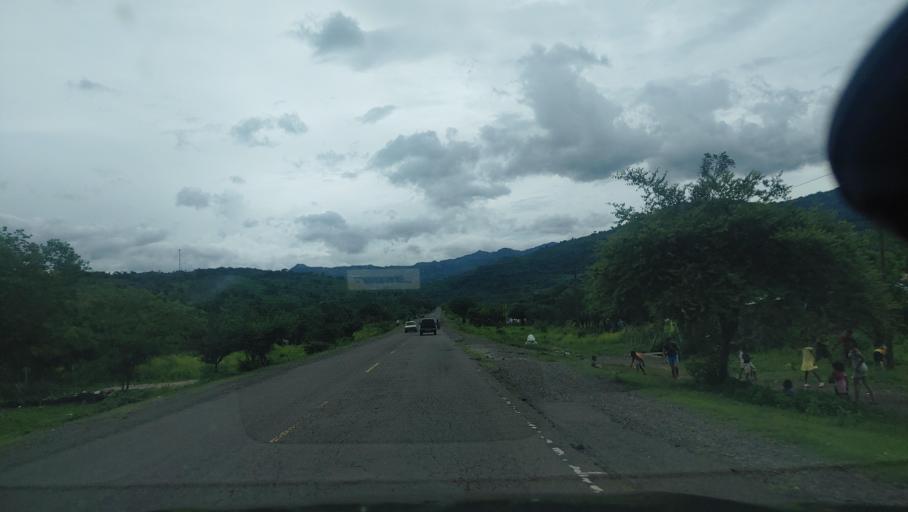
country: HN
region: Choluteca
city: Santa Ana de Yusguare
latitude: 13.3593
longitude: -87.0943
